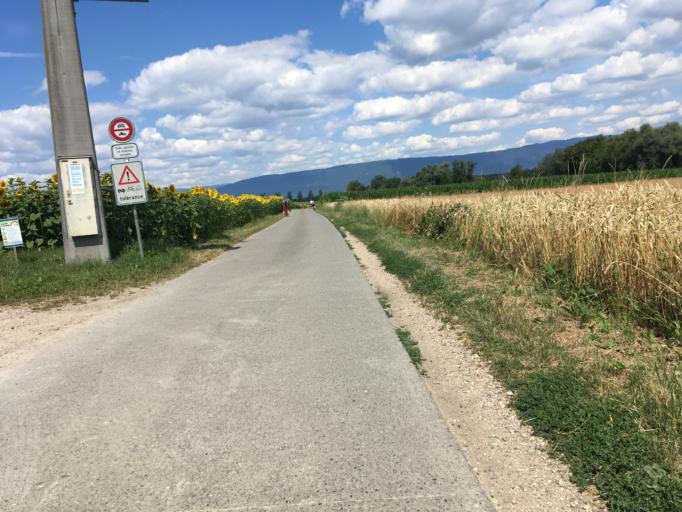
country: CH
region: Fribourg
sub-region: See District
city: Bas-Vully
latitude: 46.9683
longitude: 7.1062
